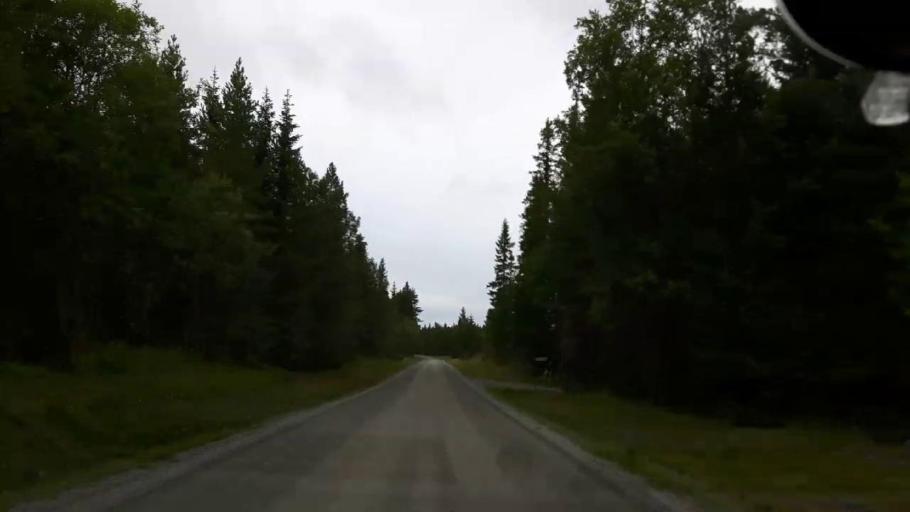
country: SE
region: Jaemtland
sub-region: OEstersunds Kommun
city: Ostersund
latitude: 63.1224
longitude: 14.5382
